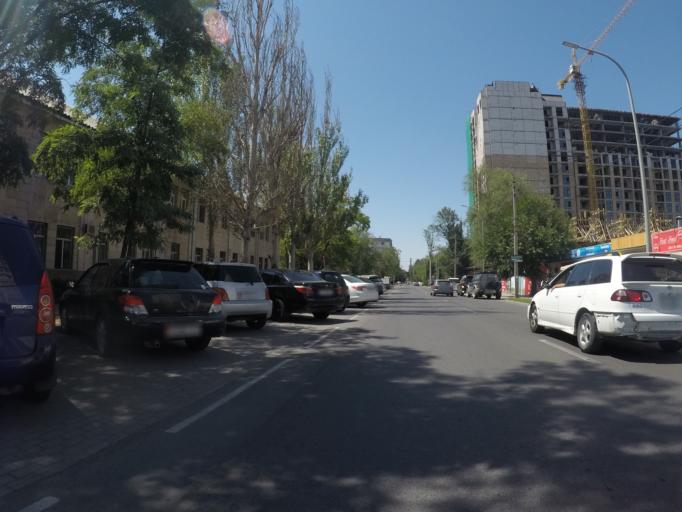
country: KG
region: Chuy
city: Bishkek
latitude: 42.8678
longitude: 74.5857
